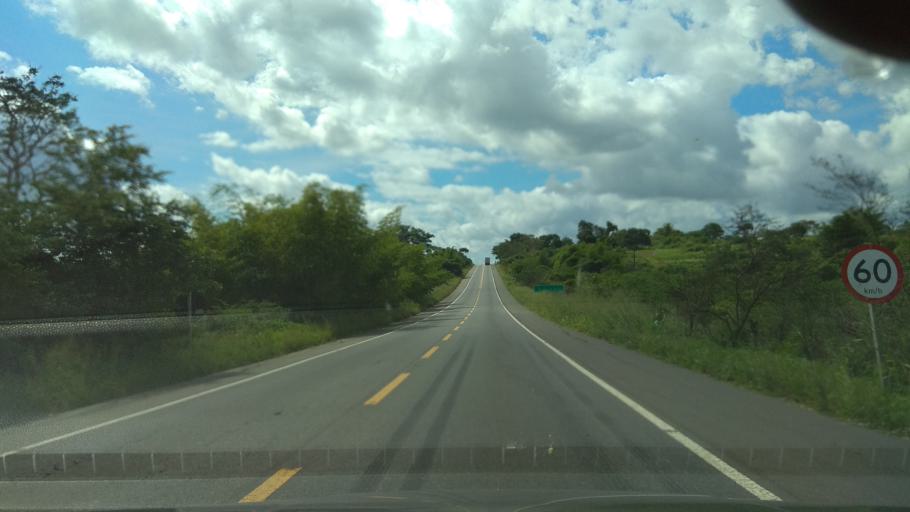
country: BR
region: Bahia
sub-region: Sao Goncalo Dos Campos
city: Sao Goncalo dos Campos
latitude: -12.4354
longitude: -38.9158
